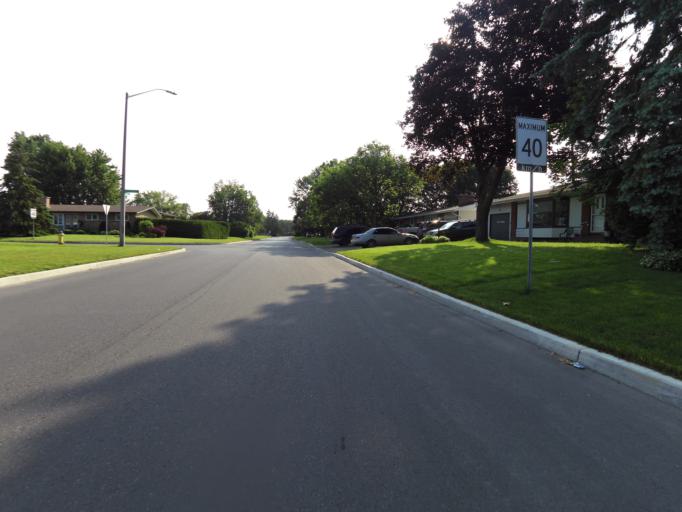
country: CA
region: Ontario
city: Ottawa
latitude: 45.3607
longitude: -75.7218
